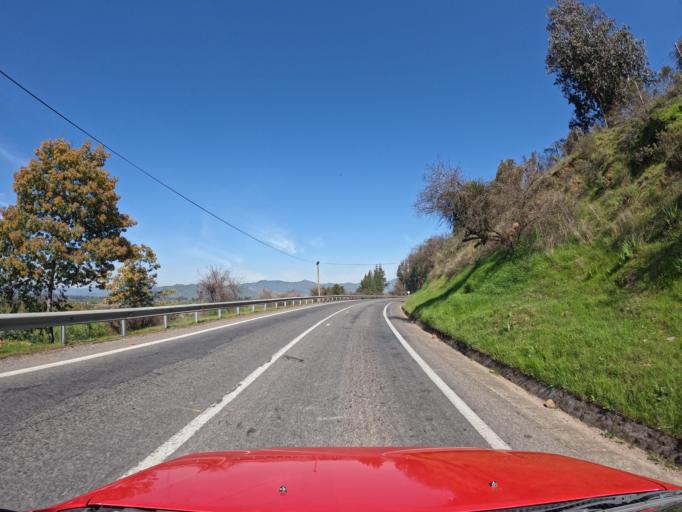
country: CL
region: Maule
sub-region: Provincia de Talca
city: Talca
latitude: -35.0870
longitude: -71.6447
